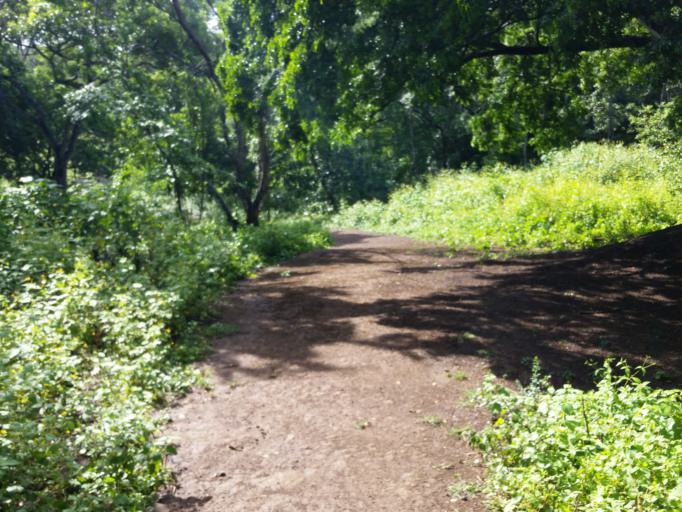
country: NI
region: Managua
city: Managua
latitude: 12.0869
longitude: -86.2552
